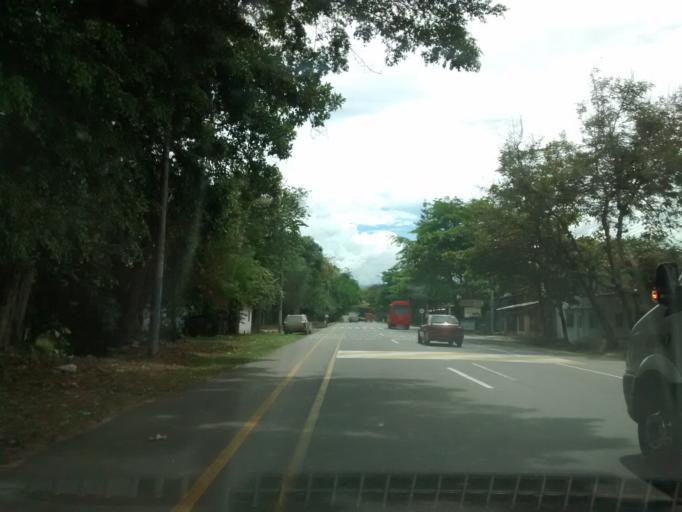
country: CO
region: Tolima
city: Ibague
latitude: 4.4024
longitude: -75.1517
